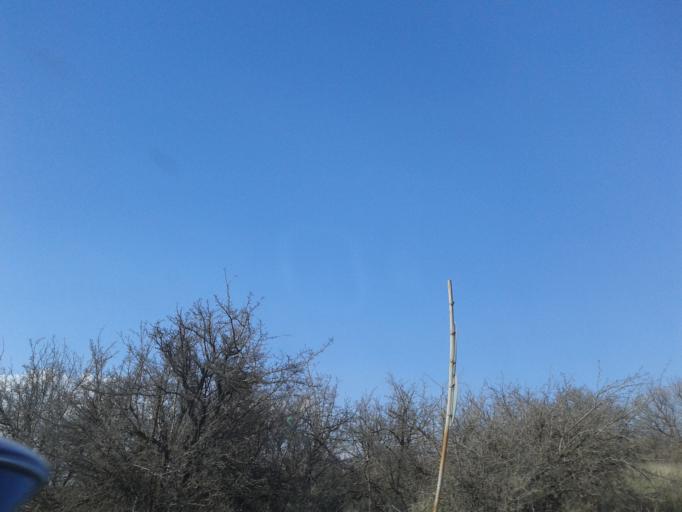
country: RU
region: Volgograd
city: Volgograd
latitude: 48.6300
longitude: 44.3978
